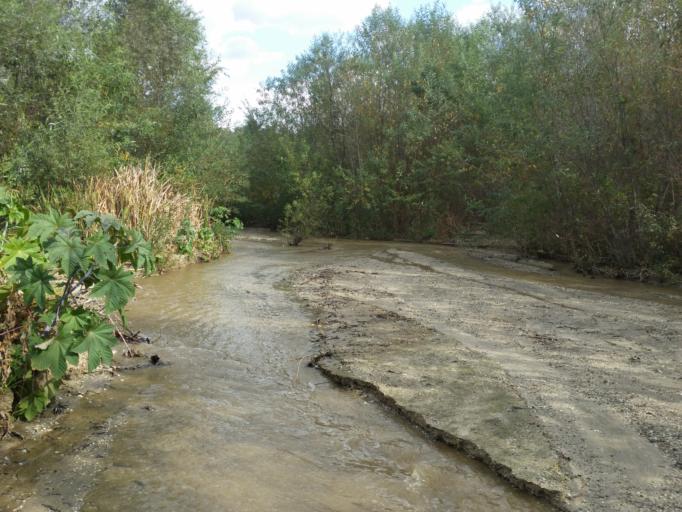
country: US
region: California
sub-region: San Bernardino County
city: Redlands
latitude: 34.0231
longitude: -117.1929
